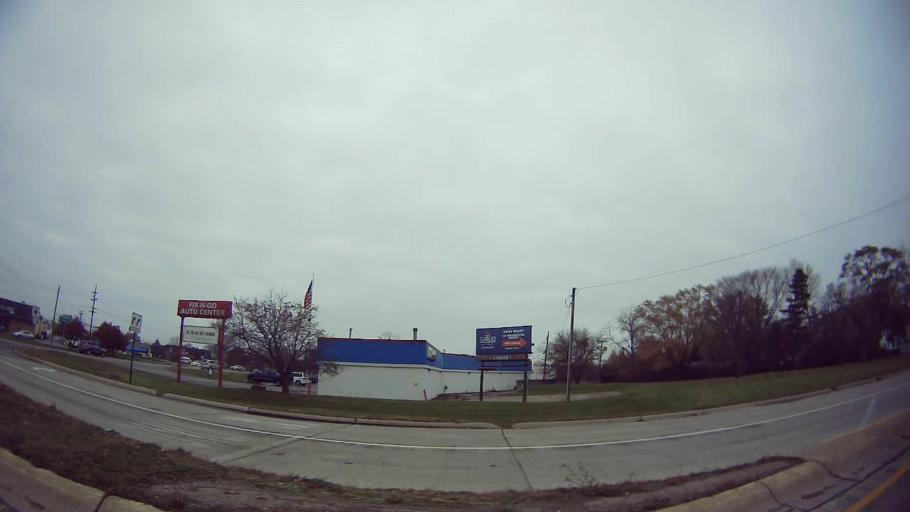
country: US
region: Michigan
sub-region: Oakland County
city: Clawson
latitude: 42.5556
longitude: -83.1283
